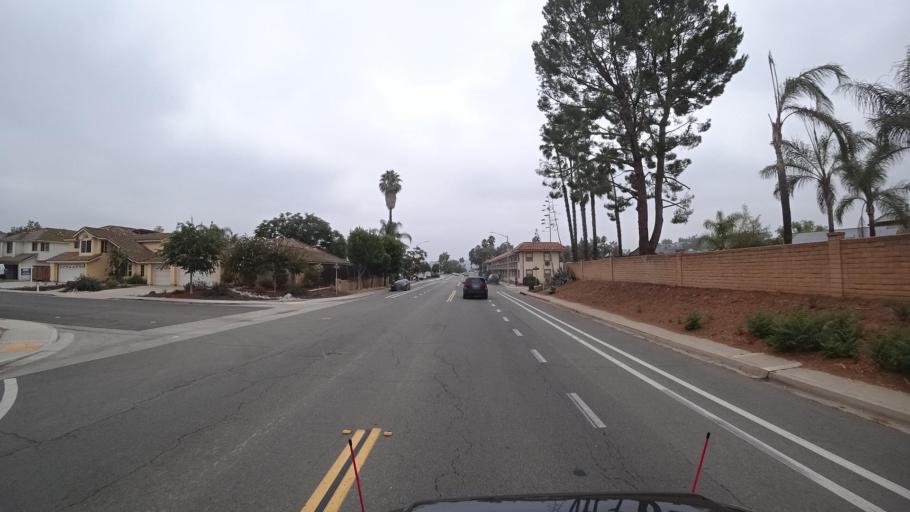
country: US
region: California
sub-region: San Diego County
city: Poway
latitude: 32.9563
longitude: -117.0213
